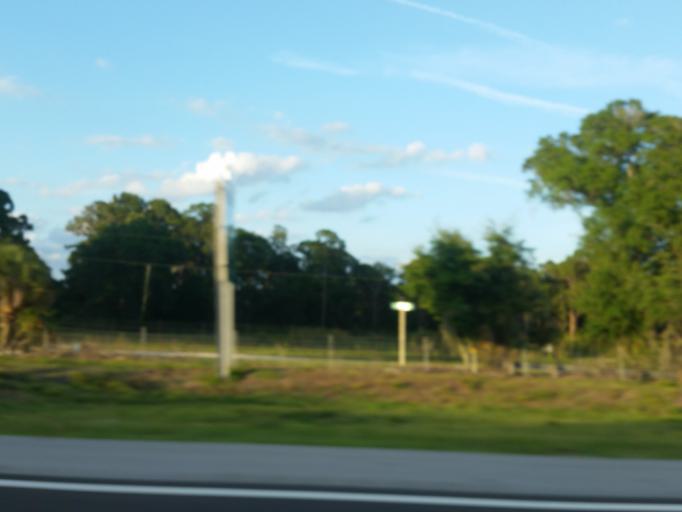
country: US
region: Florida
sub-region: Sarasota County
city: Venice Gardens
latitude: 27.1192
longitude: -82.3928
